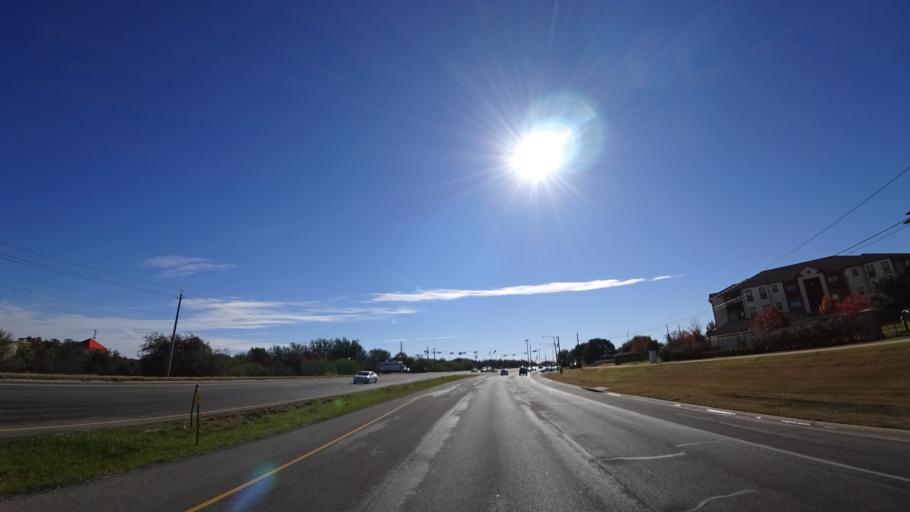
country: US
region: Texas
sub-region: Williamson County
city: Jollyville
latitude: 30.4826
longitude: -97.7679
